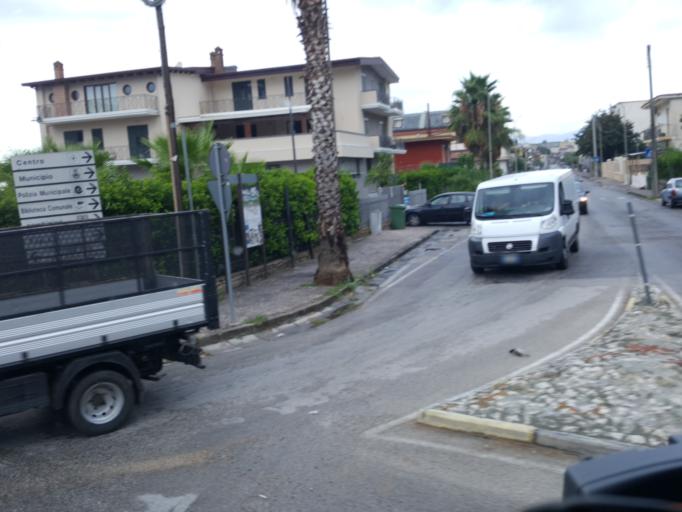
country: IT
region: Campania
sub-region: Provincia di Napoli
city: Palma Campania
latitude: 40.8565
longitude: 14.5535
